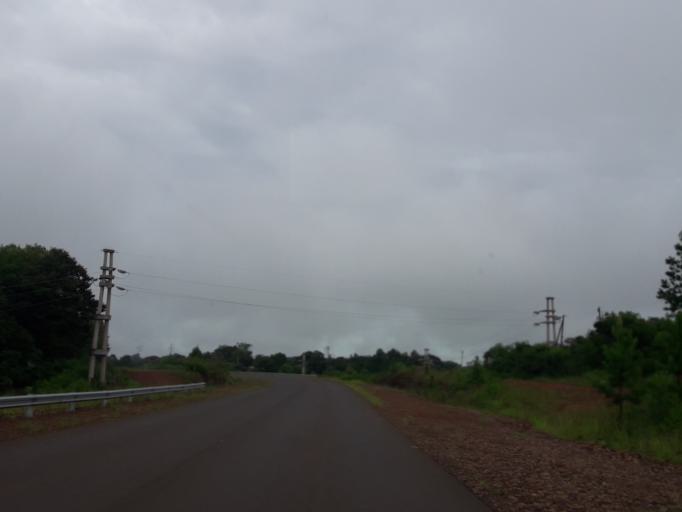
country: AR
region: Misiones
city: Bernardo de Irigoyen
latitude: -26.4209
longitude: -53.8353
